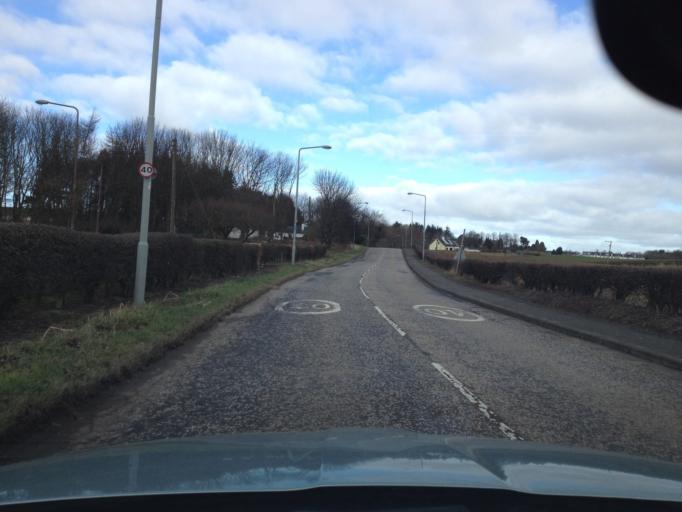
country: GB
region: Scotland
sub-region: West Lothian
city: Mid Calder
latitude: 55.8984
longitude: -3.4845
